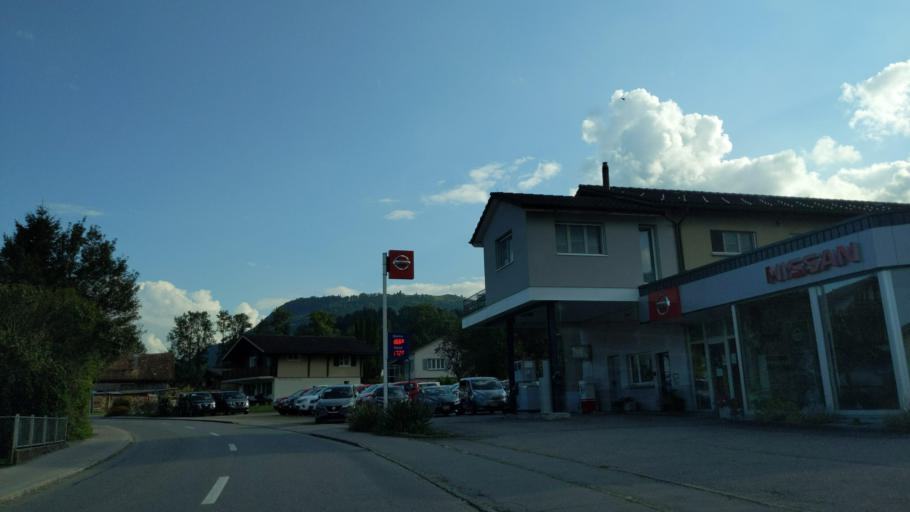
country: CH
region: Saint Gallen
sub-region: Wahlkreis Rheintal
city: Eichberg
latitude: 47.3408
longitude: 9.5310
